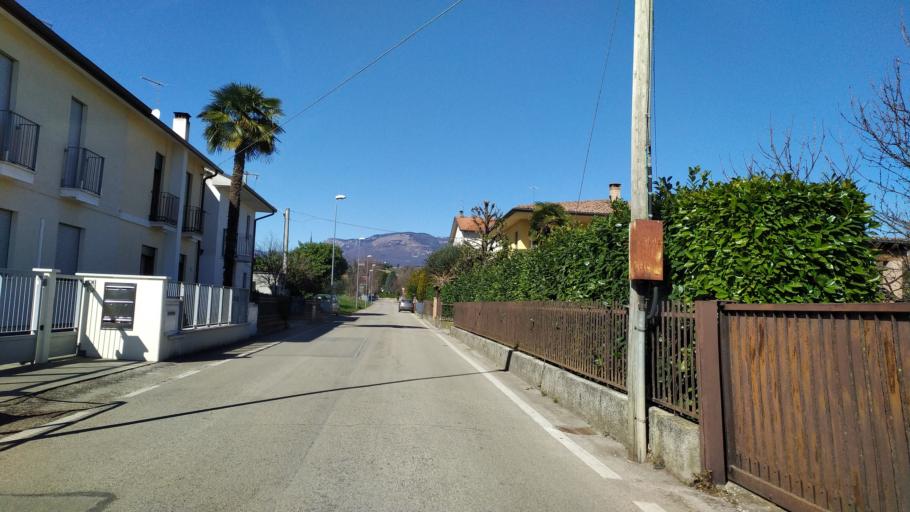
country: IT
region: Veneto
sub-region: Provincia di Vicenza
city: Breganze
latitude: 45.7030
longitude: 11.5728
